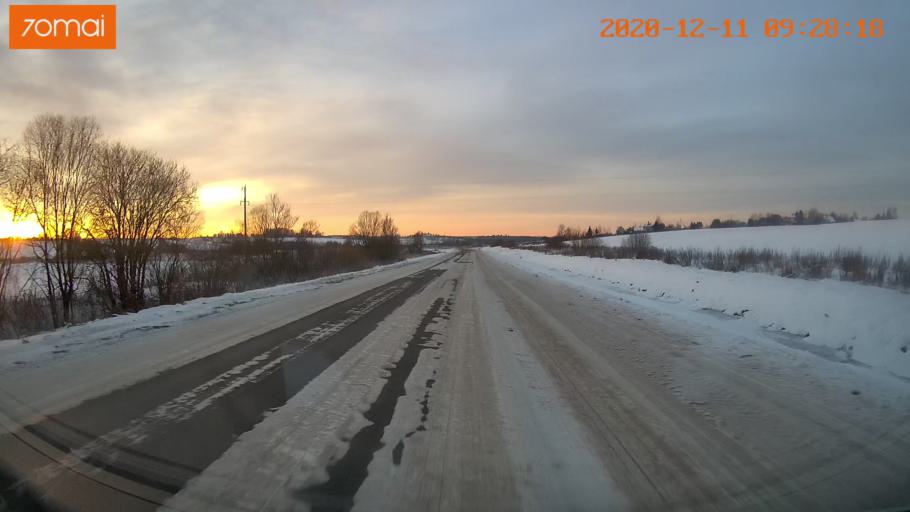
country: RU
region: Vologda
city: Vologda
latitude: 59.1548
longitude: 40.0092
